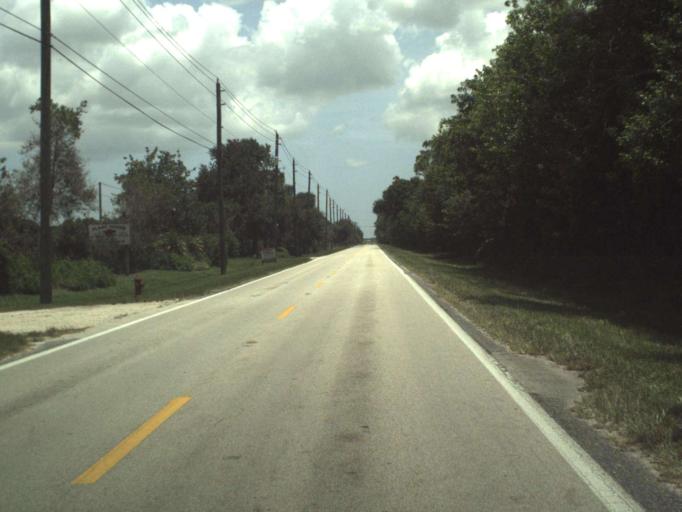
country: US
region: Florida
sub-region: Saint Lucie County
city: Fort Pierce South
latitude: 27.3744
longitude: -80.4306
